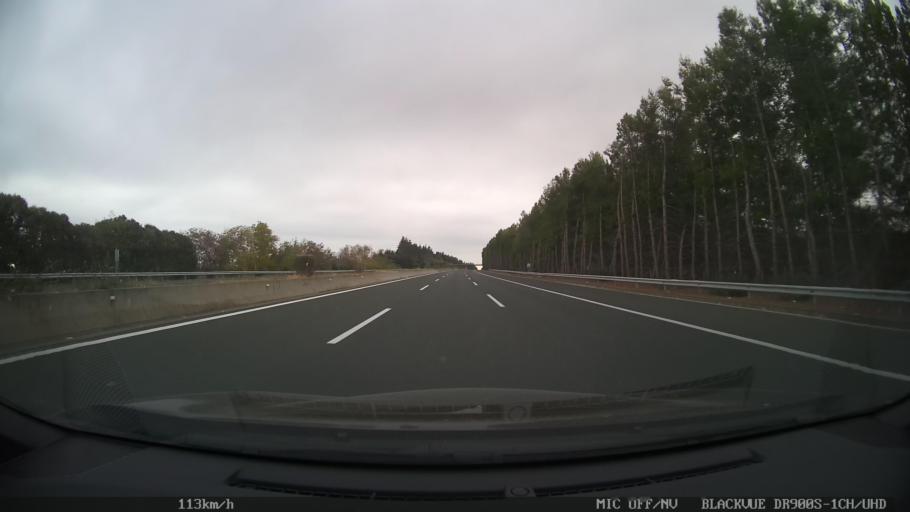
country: GR
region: Central Macedonia
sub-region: Nomos Pierias
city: Kitros
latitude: 40.3848
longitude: 22.6061
